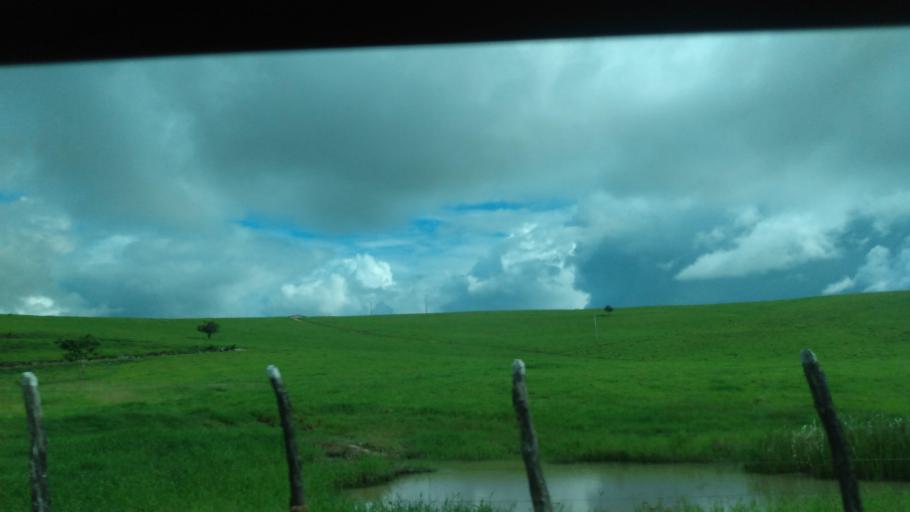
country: BR
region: Pernambuco
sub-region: Quipapa
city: Quipapa
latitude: -8.7784
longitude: -35.9209
